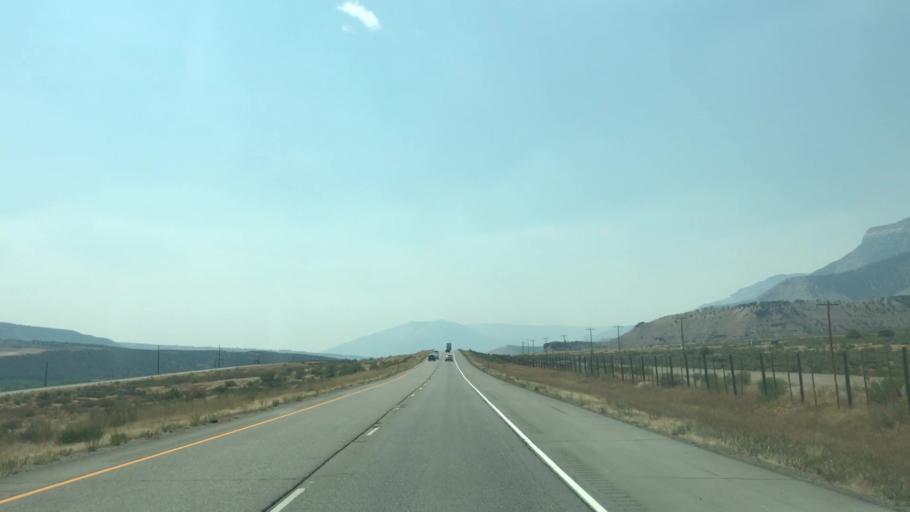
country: US
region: Colorado
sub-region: Garfield County
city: Rifle
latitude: 39.5035
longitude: -107.9018
